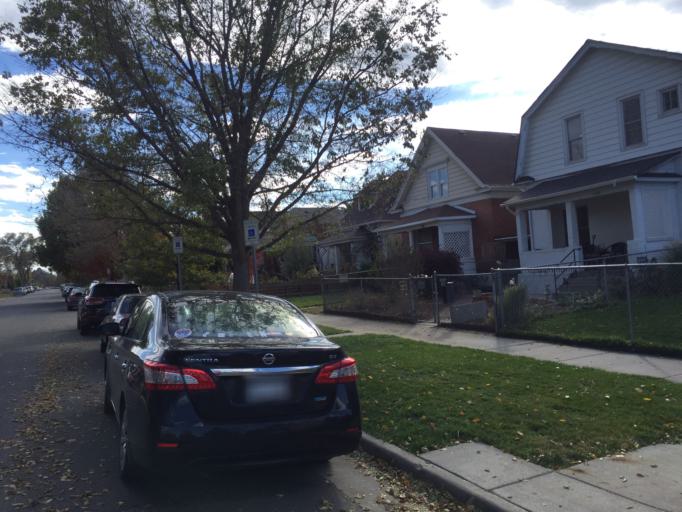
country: US
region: Colorado
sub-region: Denver County
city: Denver
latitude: 39.7643
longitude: -104.9647
